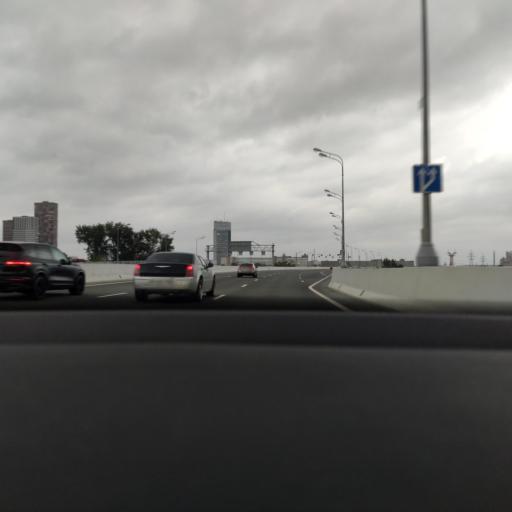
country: RU
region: Moskovskaya
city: Bogorodskoye
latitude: 55.8125
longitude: 37.7447
